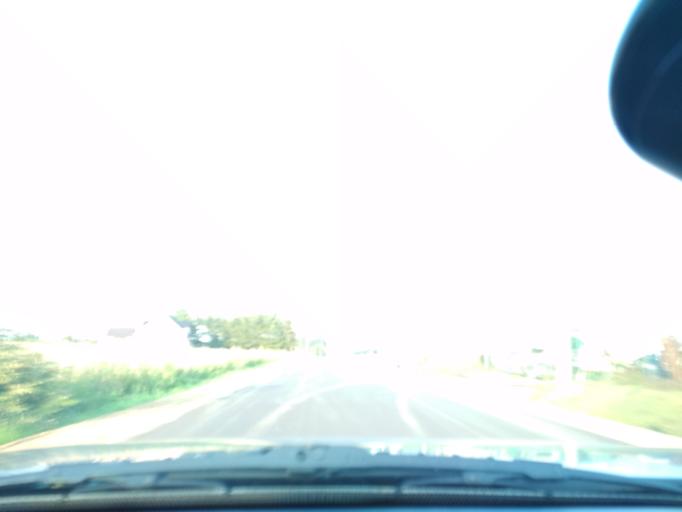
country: PL
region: Lesser Poland Voivodeship
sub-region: Powiat olkuski
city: Wolbrom
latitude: 50.4080
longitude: 19.7790
